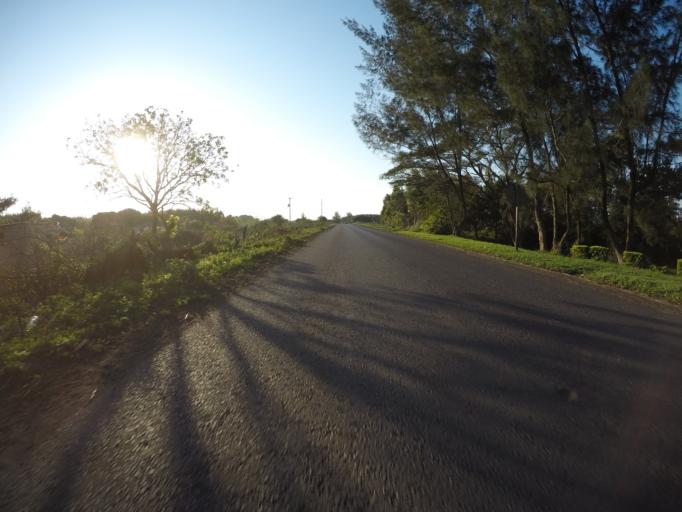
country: ZA
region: KwaZulu-Natal
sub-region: uThungulu District Municipality
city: KwaMbonambi
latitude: -28.6871
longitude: 32.2066
